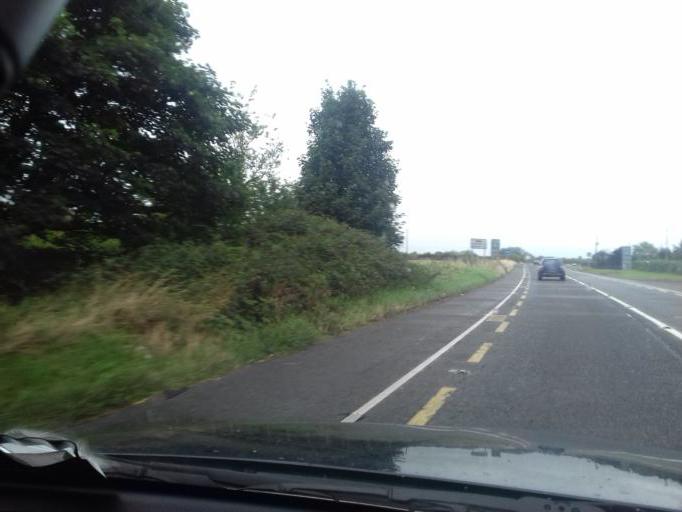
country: IE
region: Leinster
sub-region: County Carlow
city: Bagenalstown
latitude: 52.7467
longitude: -6.9679
